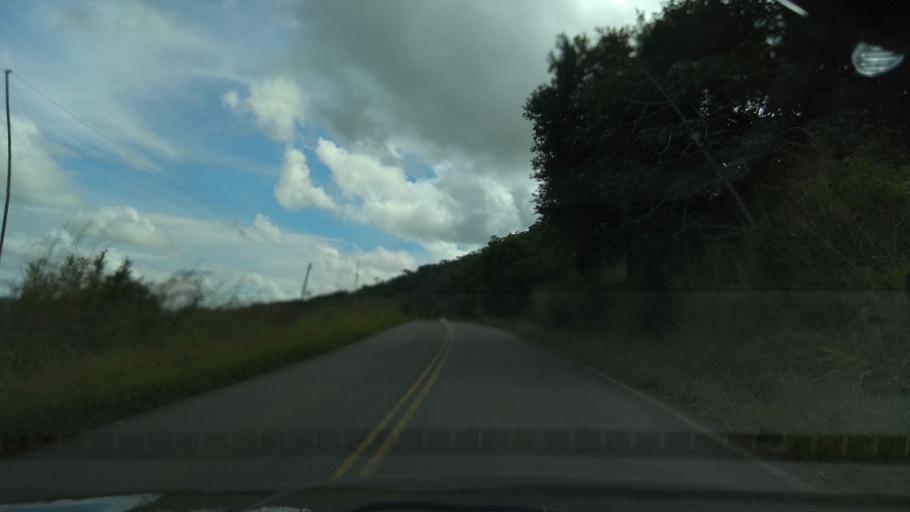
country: BR
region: Bahia
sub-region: Mutuipe
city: Mutuipe
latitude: -13.1883
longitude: -39.4413
